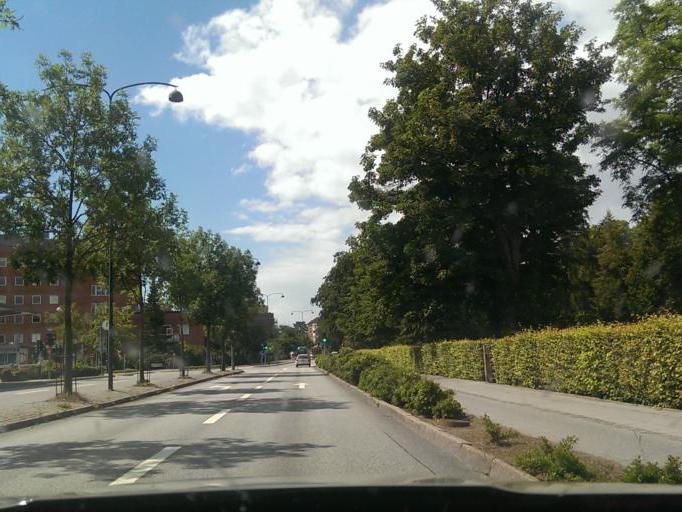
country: SE
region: Skane
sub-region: Lunds Kommun
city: Lund
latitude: 55.7136
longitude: 13.1971
